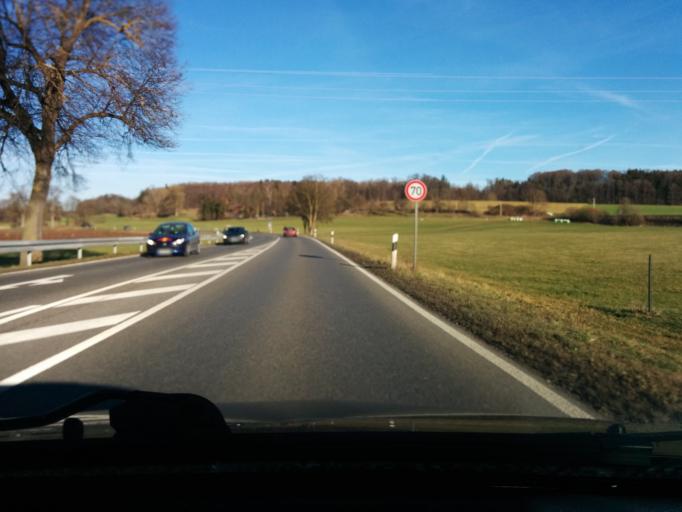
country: DE
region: Bavaria
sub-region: Upper Bavaria
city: Wielenbach
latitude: 47.8612
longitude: 11.1629
